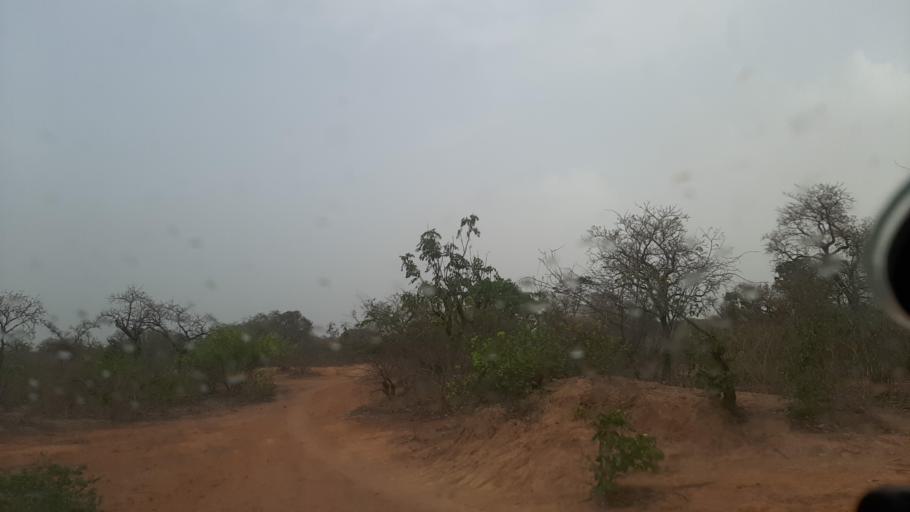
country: BF
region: Boucle du Mouhoun
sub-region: Province des Banwa
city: Salanso
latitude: 11.8639
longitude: -4.4406
